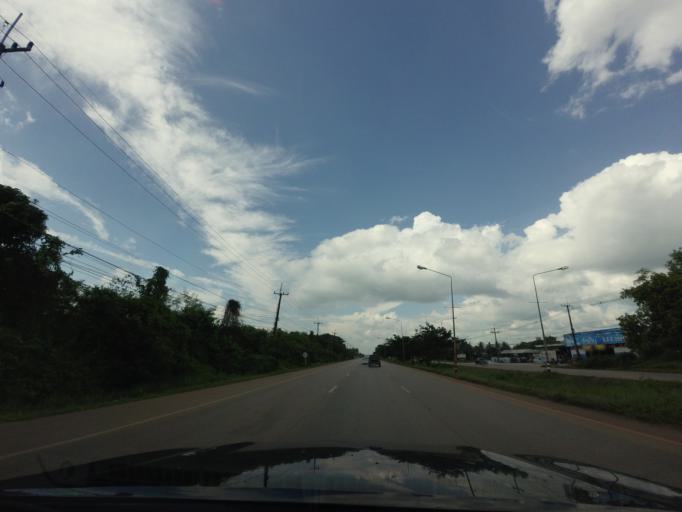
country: TH
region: Changwat Udon Thani
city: Udon Thani
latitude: 17.5370
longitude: 102.8000
